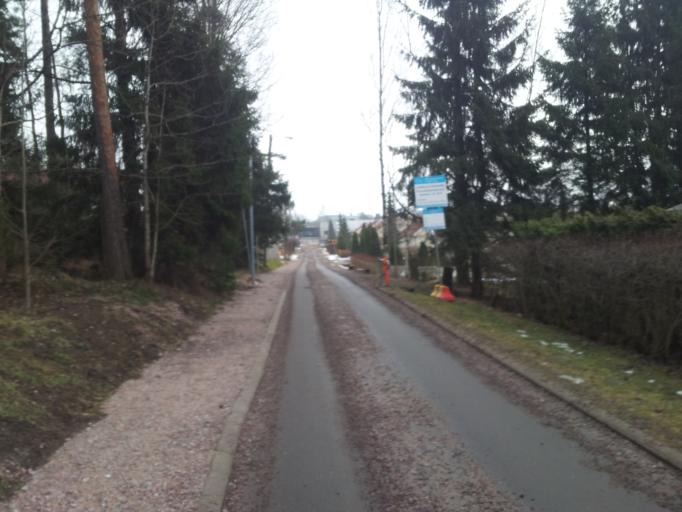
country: FI
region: Uusimaa
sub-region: Helsinki
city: Kauniainen
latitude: 60.1649
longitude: 24.7161
